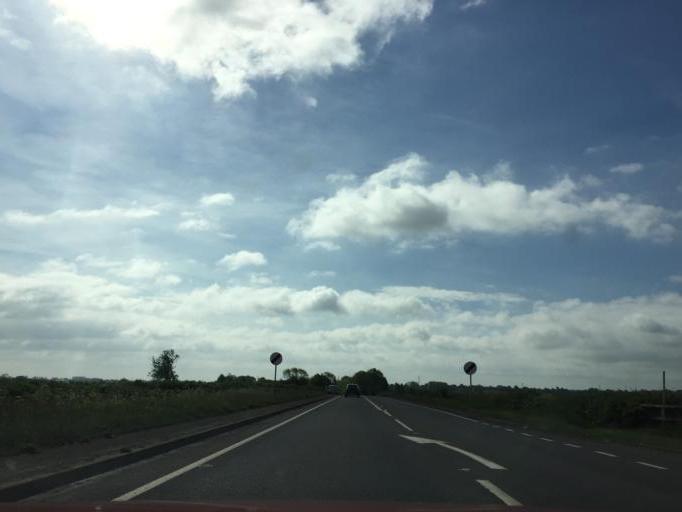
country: GB
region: England
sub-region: Northamptonshire
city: Towcester
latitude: 52.1162
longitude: -0.9610
